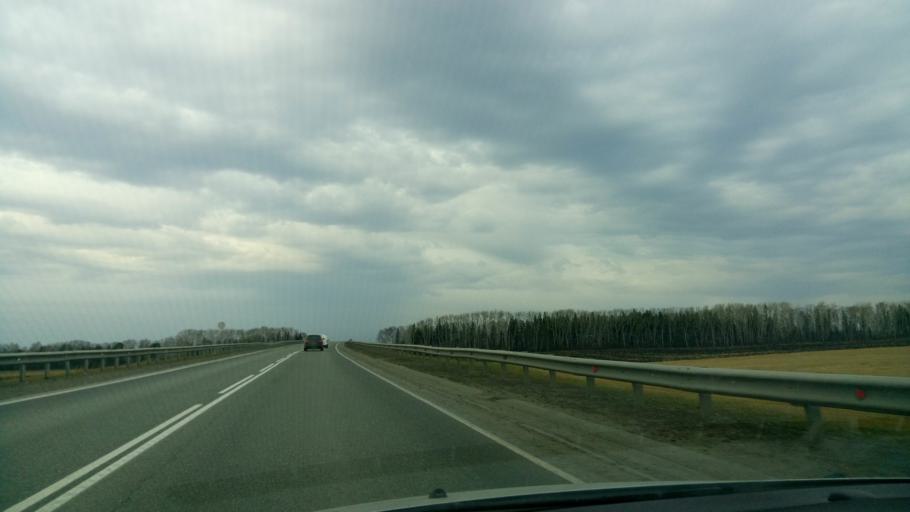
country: RU
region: Sverdlovsk
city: Kamyshlov
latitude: 56.8522
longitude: 62.8160
